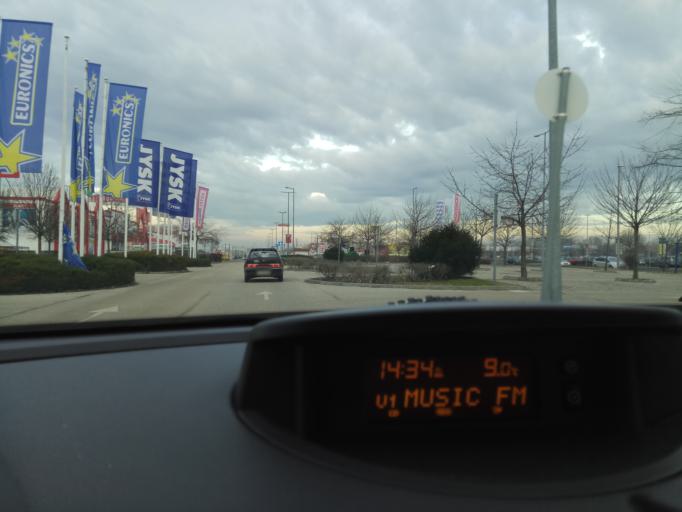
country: HU
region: Pest
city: Dunakeszi
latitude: 47.6078
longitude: 19.1138
